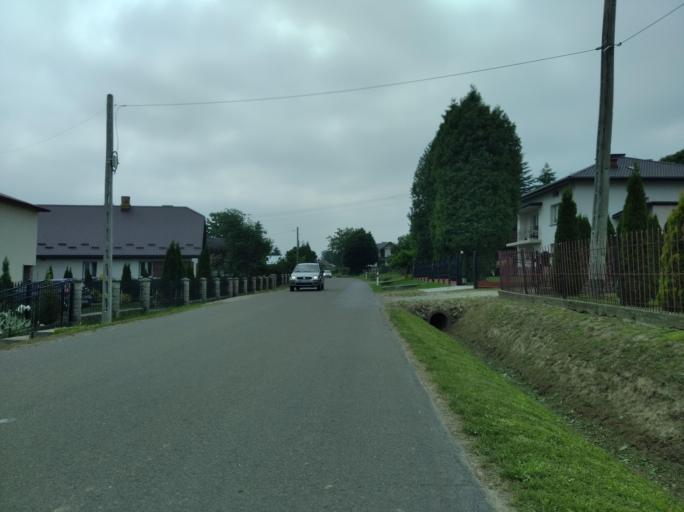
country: PL
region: Subcarpathian Voivodeship
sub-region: Powiat sanocki
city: Besko
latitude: 49.5937
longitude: 21.9362
